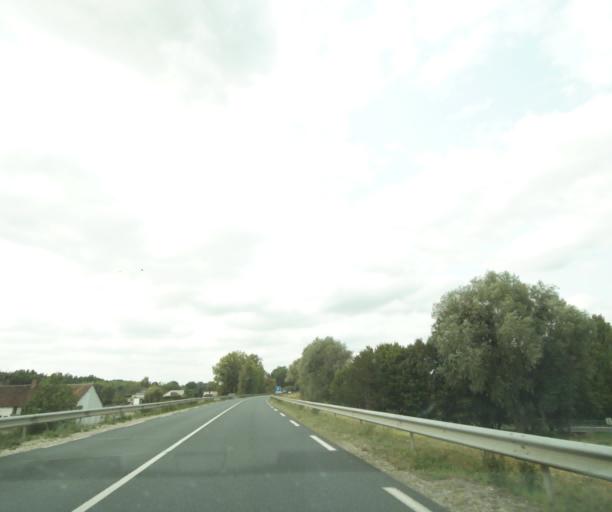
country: FR
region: Centre
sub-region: Departement de l'Indre
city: Buzancais
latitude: 46.8828
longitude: 1.4094
